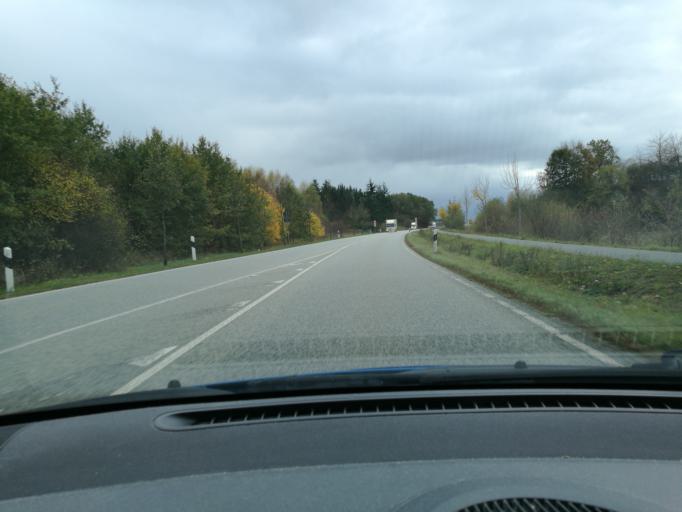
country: DE
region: Schleswig-Holstein
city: Einhaus
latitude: 53.7085
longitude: 10.7343
